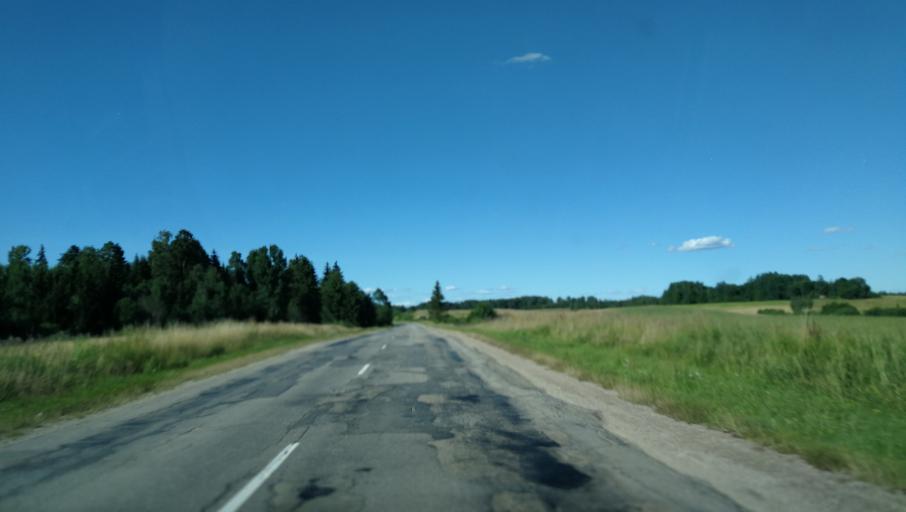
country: LV
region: Madonas Rajons
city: Madona
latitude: 56.9609
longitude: 26.0456
